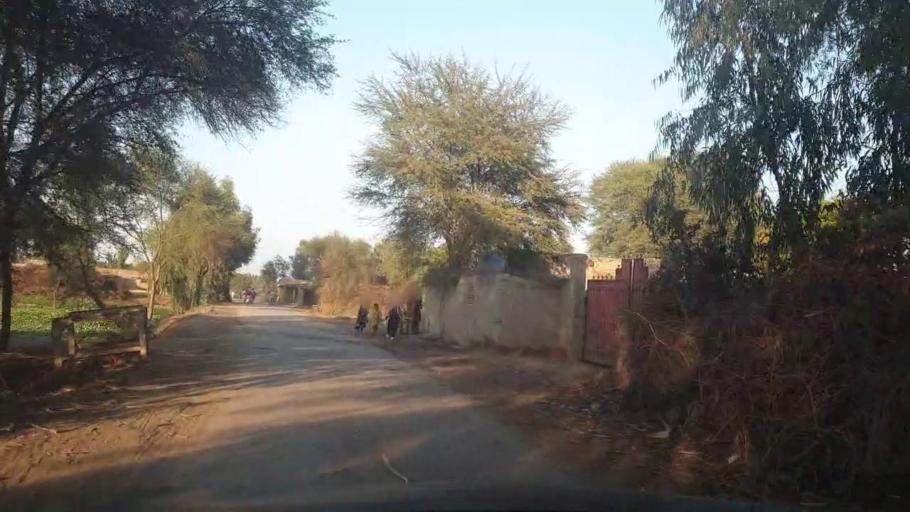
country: PK
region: Sindh
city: Ubauro
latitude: 28.1701
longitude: 69.5829
